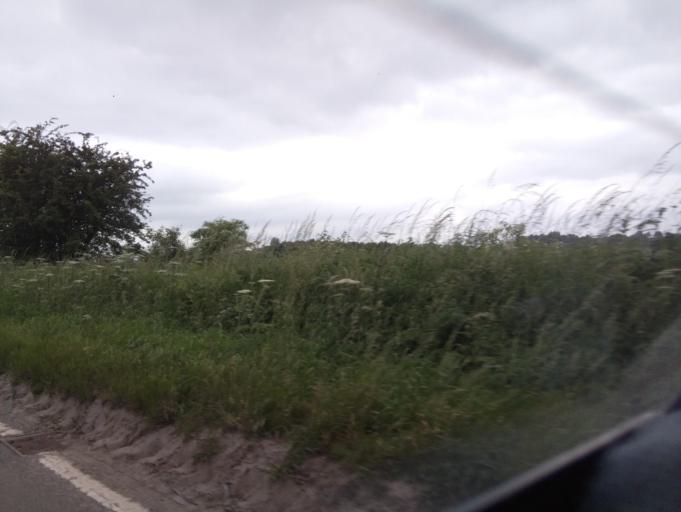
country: GB
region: England
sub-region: Staffordshire
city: Mayfield
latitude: 52.9299
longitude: -1.7636
